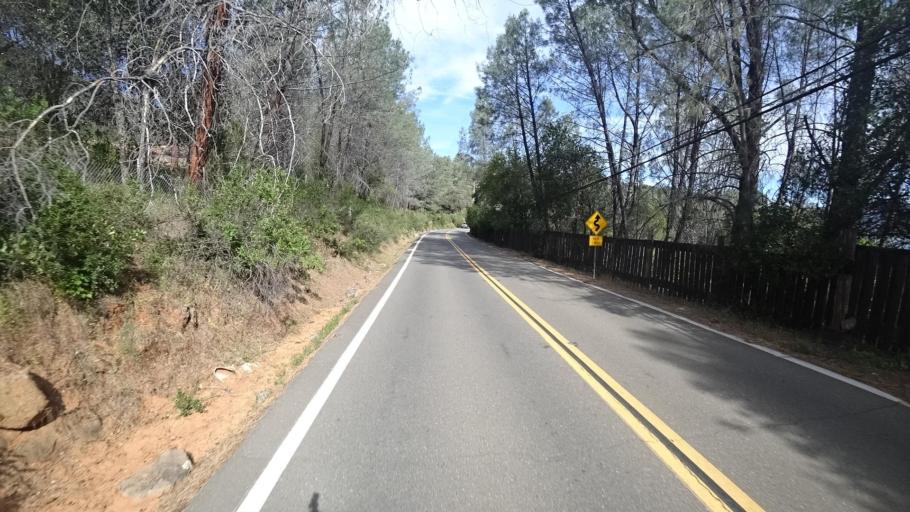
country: US
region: California
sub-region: Lake County
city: Soda Bay
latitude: 38.9862
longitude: -122.7429
